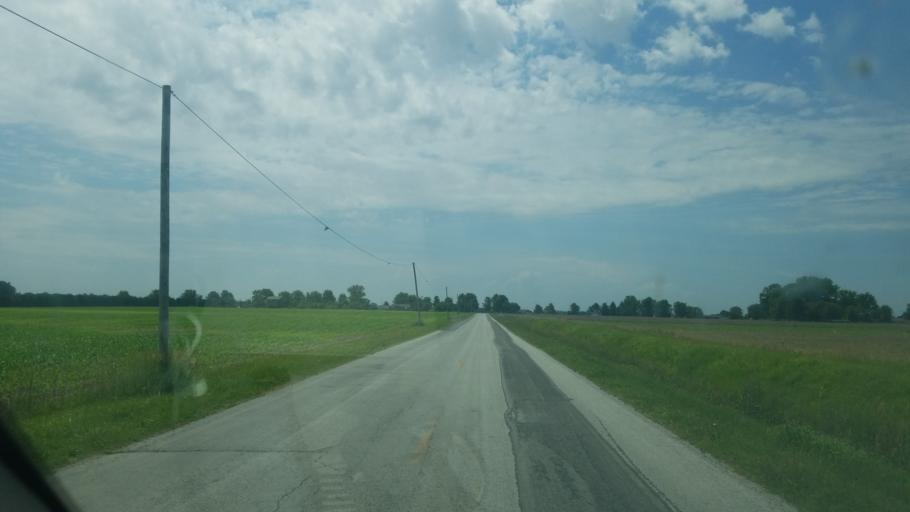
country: US
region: Ohio
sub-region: Wood County
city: North Baltimore
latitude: 41.2592
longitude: -83.5929
